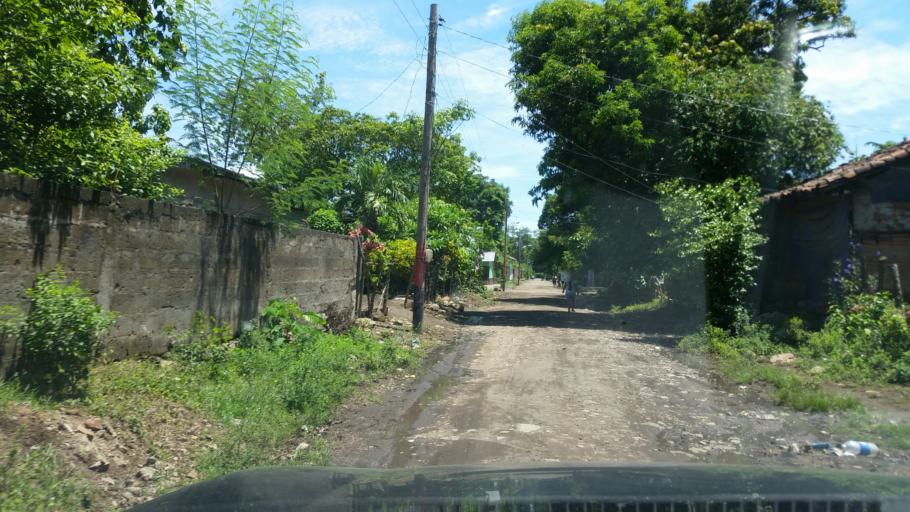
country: NI
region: Chinandega
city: Puerto Morazan
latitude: 12.7666
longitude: -87.1339
